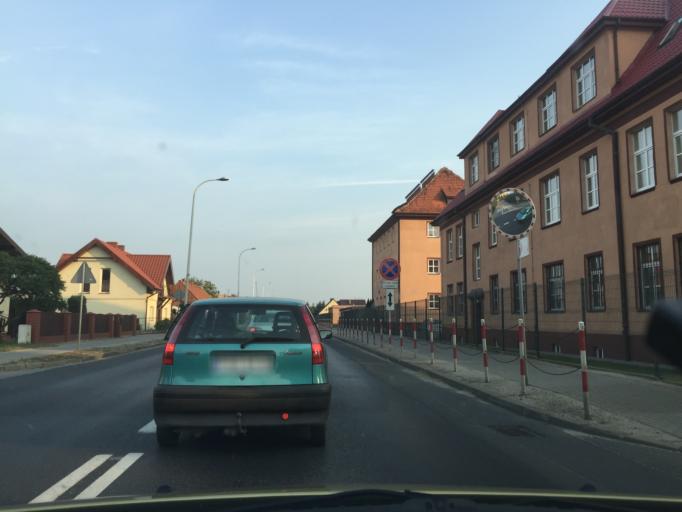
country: PL
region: Greater Poland Voivodeship
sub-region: Powiat jarocinski
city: Jarocin
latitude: 51.9622
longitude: 17.5121
